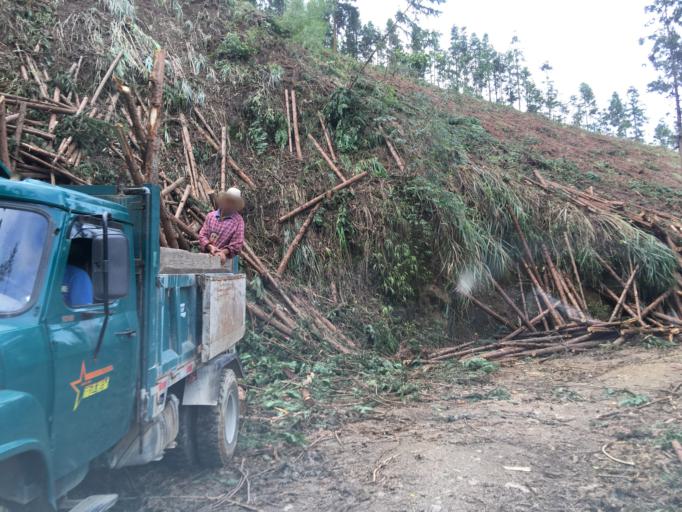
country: CN
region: Guangxi Zhuangzu Zizhiqu
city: Xinzhou
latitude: 24.8767
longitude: 105.8457
